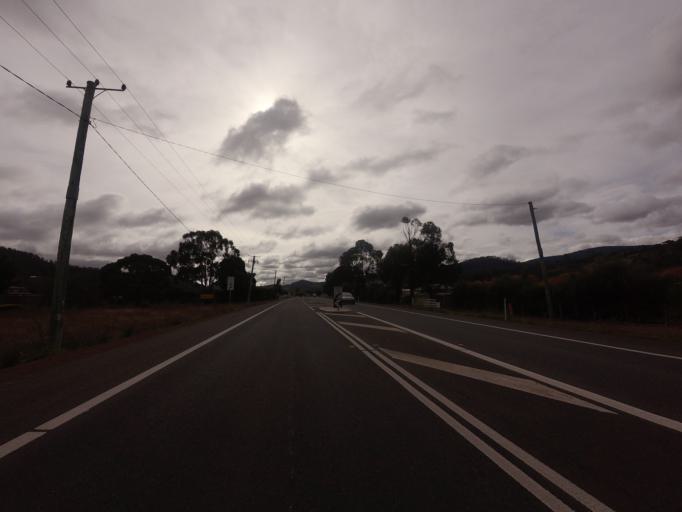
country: AU
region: Tasmania
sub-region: Brighton
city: Bridgewater
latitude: -42.6206
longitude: 147.2221
